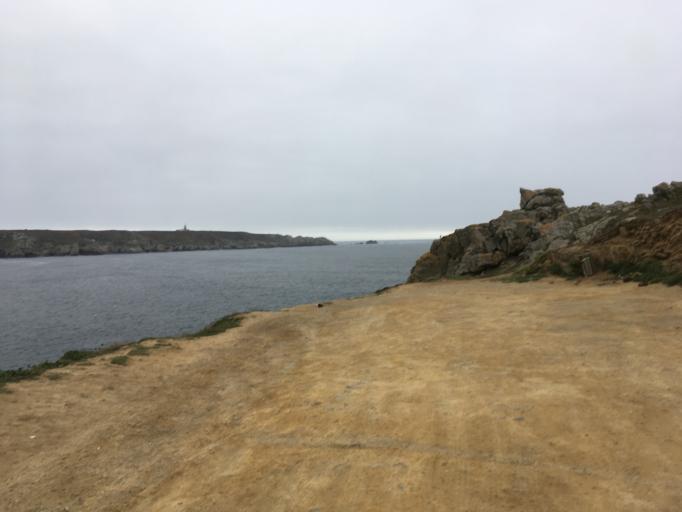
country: FR
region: Brittany
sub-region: Departement du Finistere
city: Plogoff
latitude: 48.0533
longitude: -4.7123
